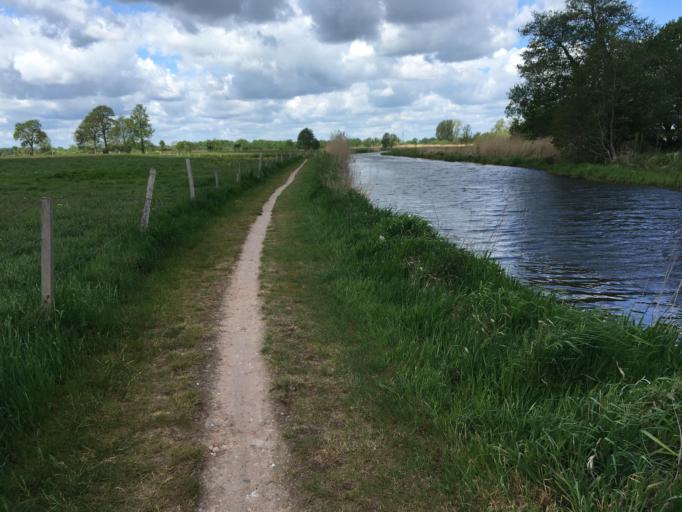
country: DE
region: Lower Saxony
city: Brietlingen
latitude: 53.3315
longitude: 10.4879
